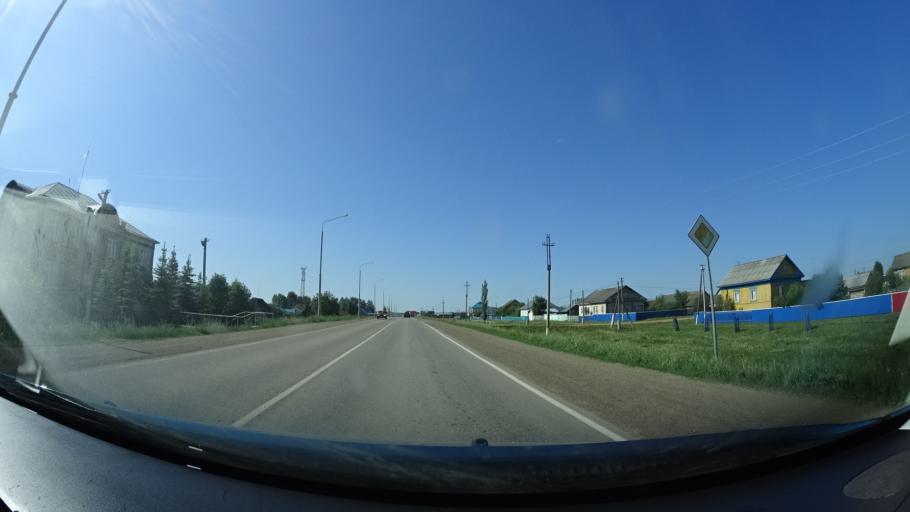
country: RU
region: Bashkortostan
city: Starobaltachevo
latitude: 56.0118
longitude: 55.9058
